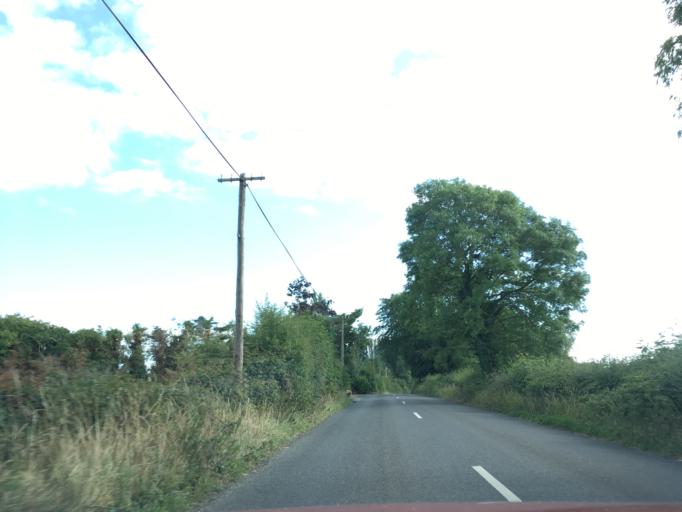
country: IE
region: Munster
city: Cashel
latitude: 52.4601
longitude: -7.9164
